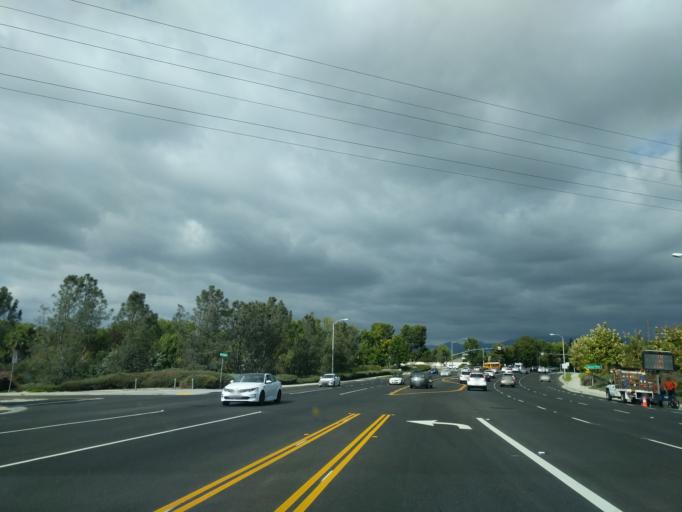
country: US
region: California
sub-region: Orange County
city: Laguna Hills
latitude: 33.5902
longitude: -117.7145
